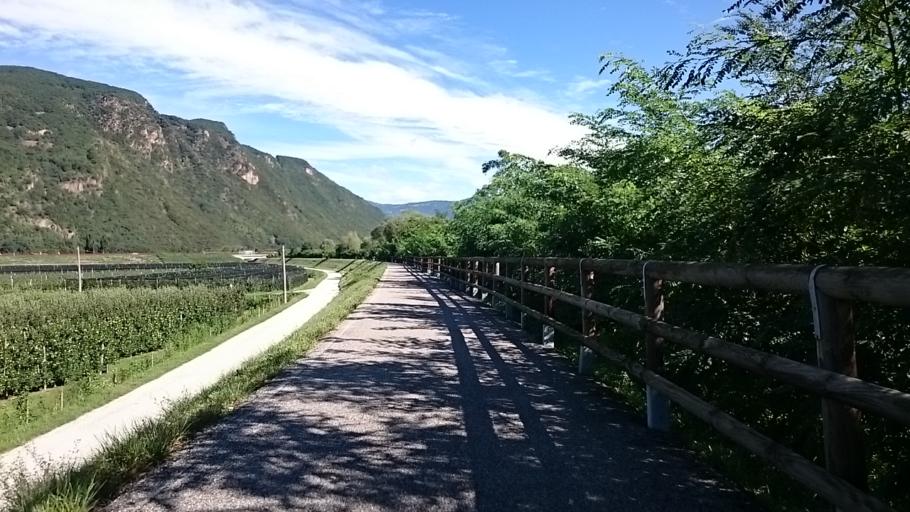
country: IT
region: Trentino-Alto Adige
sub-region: Bolzano
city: Vadena
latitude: 46.4162
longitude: 11.3148
